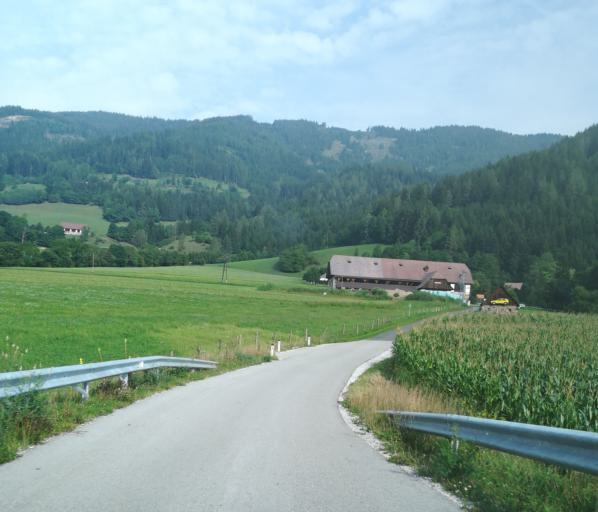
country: AT
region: Styria
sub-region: Politischer Bezirk Murtal
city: Sankt Georgen ob Judenburg
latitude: 47.2129
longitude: 14.4635
